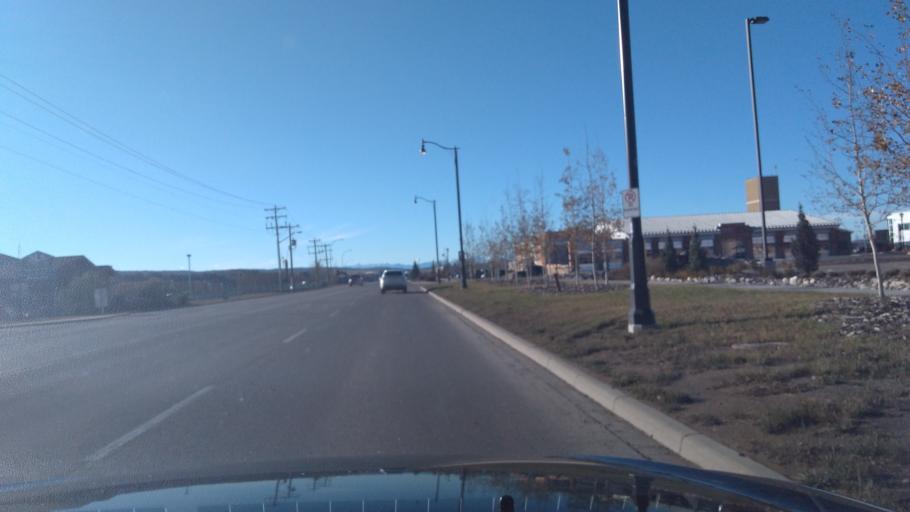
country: CA
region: Alberta
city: Cochrane
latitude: 51.1833
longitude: -114.4718
